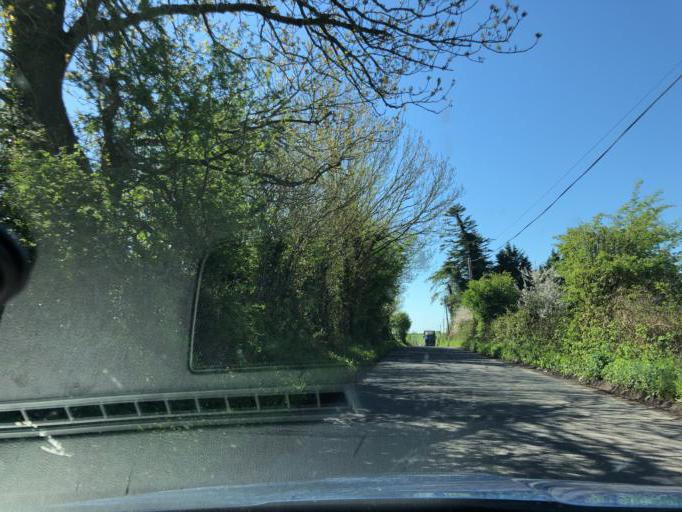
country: IE
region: Connaught
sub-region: County Galway
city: Portumna
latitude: 53.1622
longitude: -8.2938
